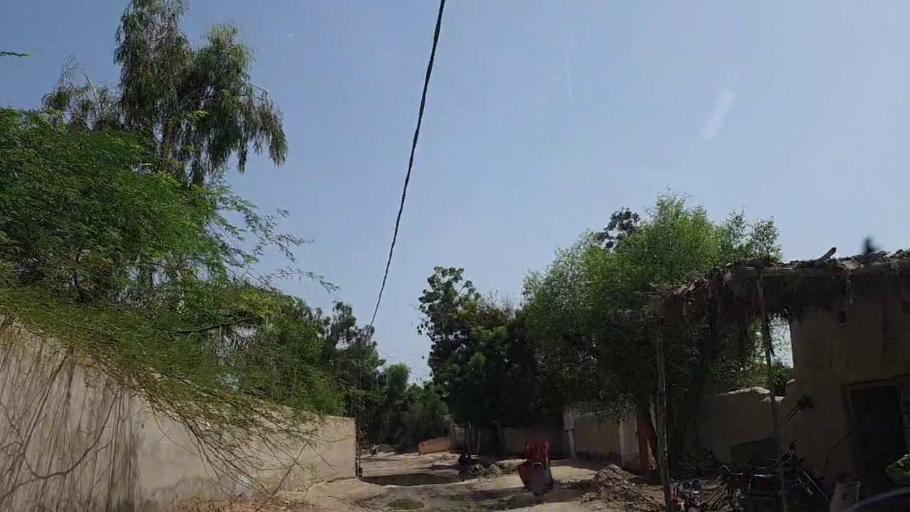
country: PK
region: Sindh
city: Tharu Shah
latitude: 27.0168
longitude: 68.1228
